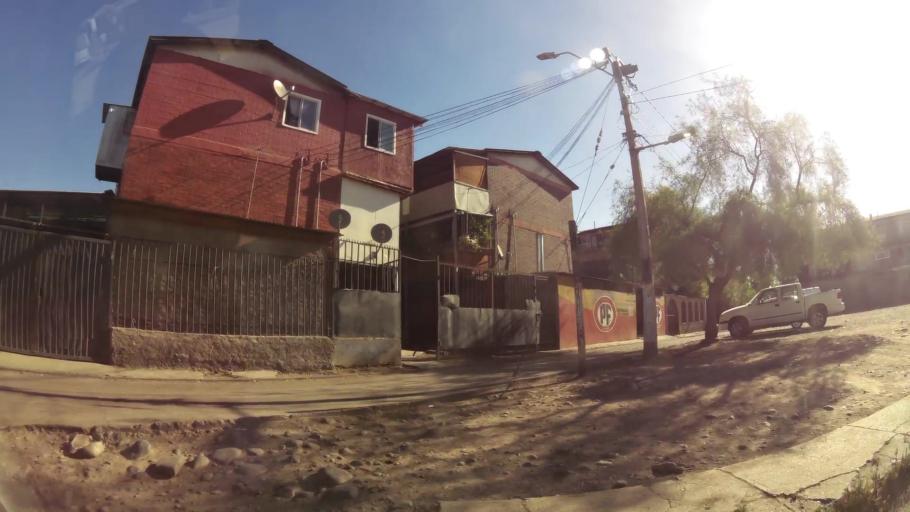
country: CL
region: Santiago Metropolitan
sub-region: Provincia de Maipo
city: San Bernardo
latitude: -33.5922
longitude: -70.6831
